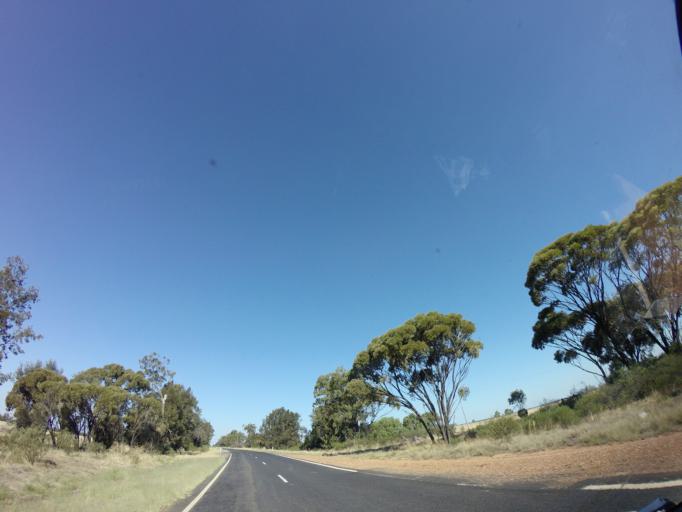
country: AU
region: New South Wales
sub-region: Gilgandra
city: Gilgandra
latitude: -31.6625
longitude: 148.4177
